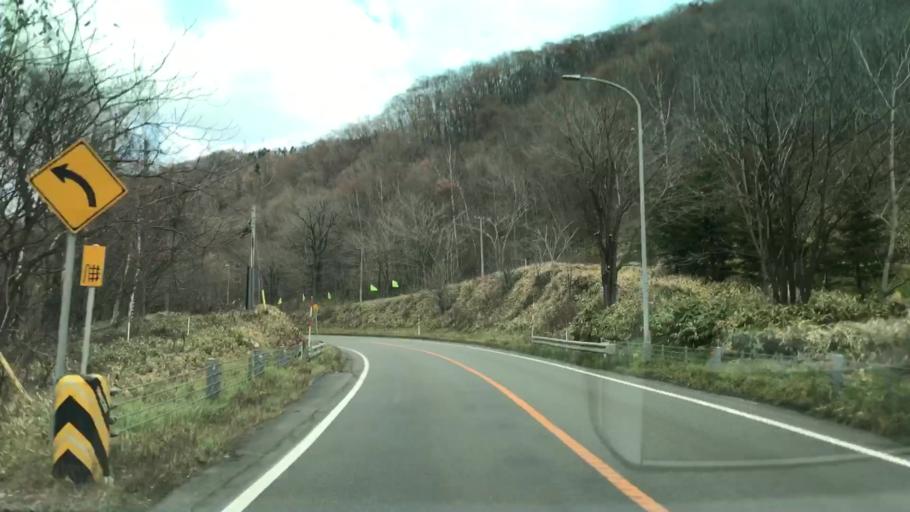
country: JP
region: Hokkaido
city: Shizunai-furukawacho
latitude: 42.8152
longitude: 142.4209
